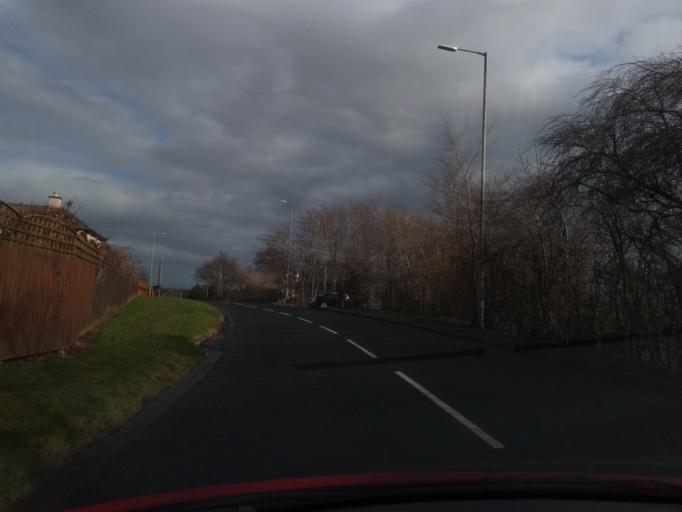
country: GB
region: Scotland
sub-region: The Scottish Borders
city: Kelso
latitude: 55.5885
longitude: -2.4375
